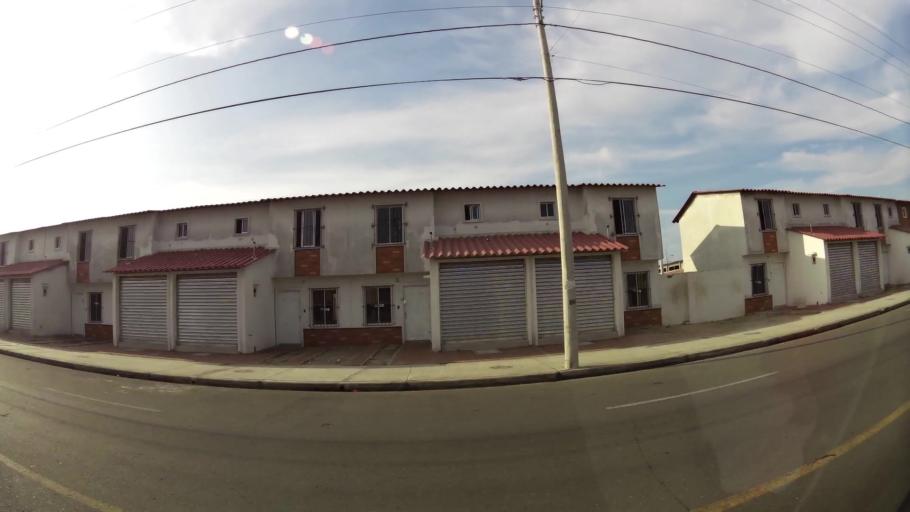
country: EC
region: Guayas
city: Eloy Alfaro
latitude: -2.0621
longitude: -79.8926
